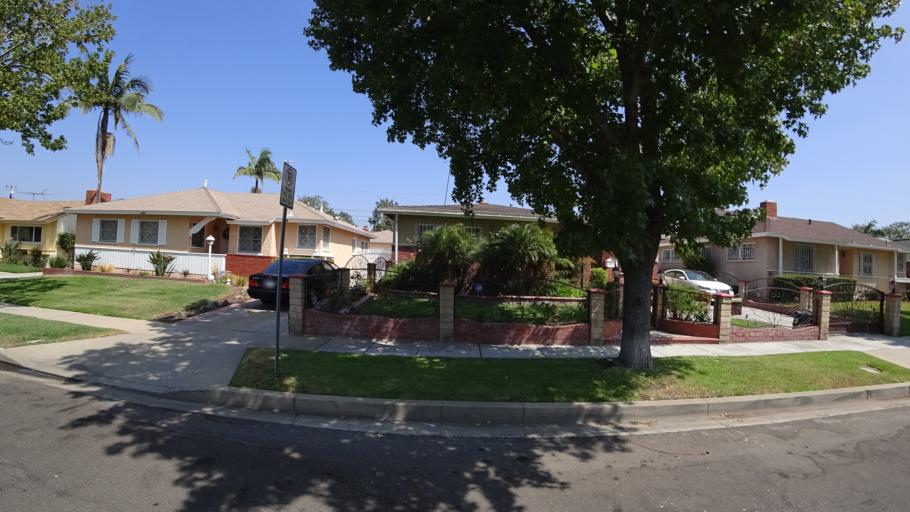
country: US
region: California
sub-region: Los Angeles County
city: Westmont
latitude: 33.9340
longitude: -118.3211
